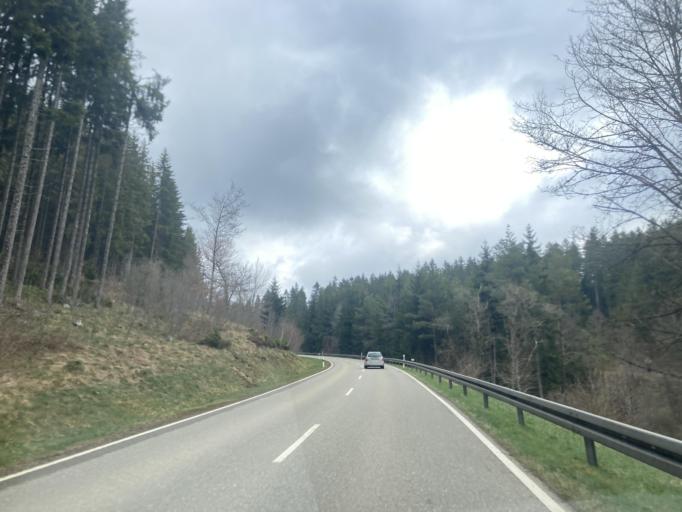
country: DE
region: Baden-Wuerttemberg
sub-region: Freiburg Region
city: Vohrenbach
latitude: 48.0358
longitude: 8.3362
